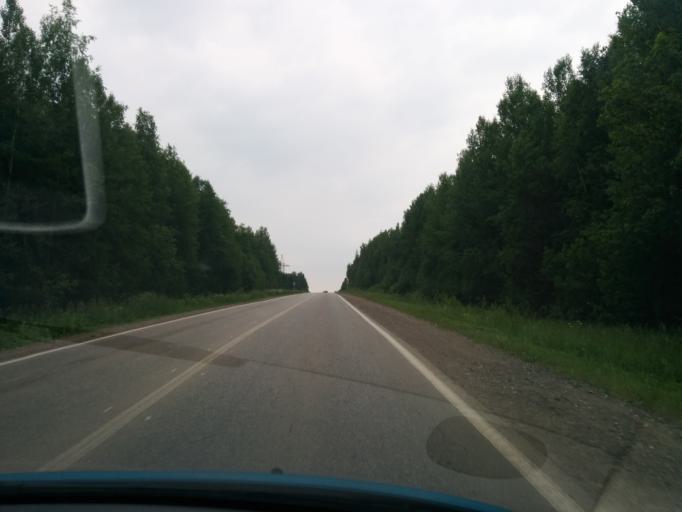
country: RU
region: Perm
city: Perm
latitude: 58.1427
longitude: 56.2660
